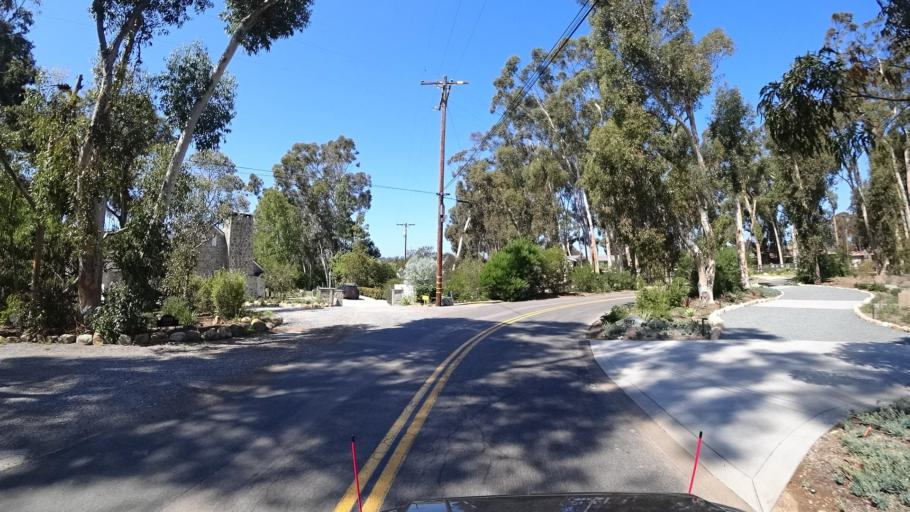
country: US
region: California
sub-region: San Diego County
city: Fairbanks Ranch
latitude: 32.9883
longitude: -117.2220
